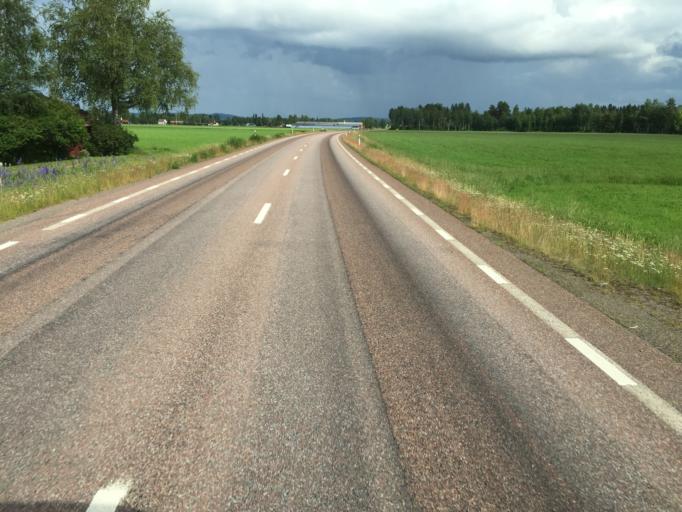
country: SE
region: Dalarna
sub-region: Vansbro Kommun
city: Jarna
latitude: 60.5543
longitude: 14.3402
